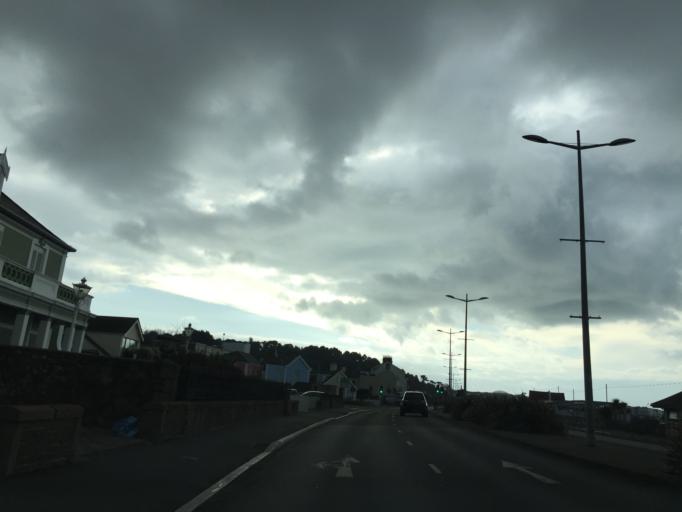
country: JE
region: St Helier
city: Saint Helier
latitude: 49.1946
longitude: -2.1297
